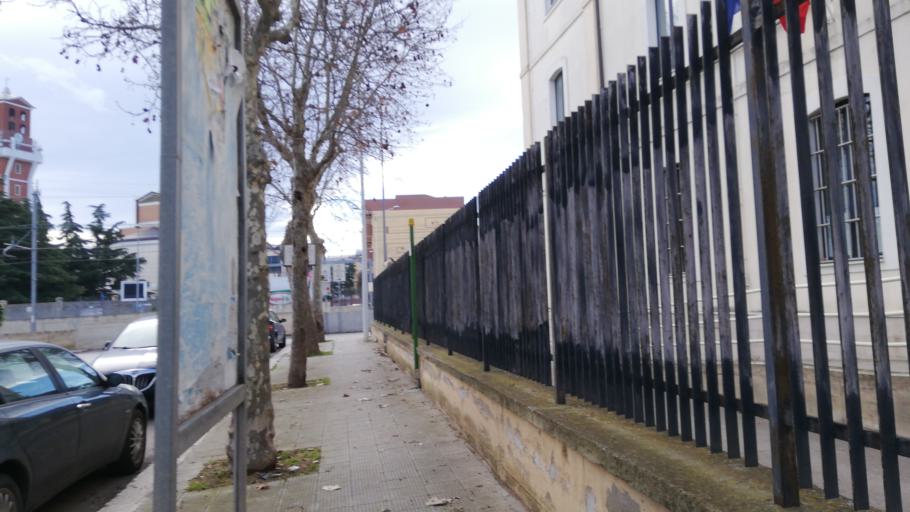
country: IT
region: Apulia
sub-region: Provincia di Bari
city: Bitonto
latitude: 41.1159
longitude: 16.6903
